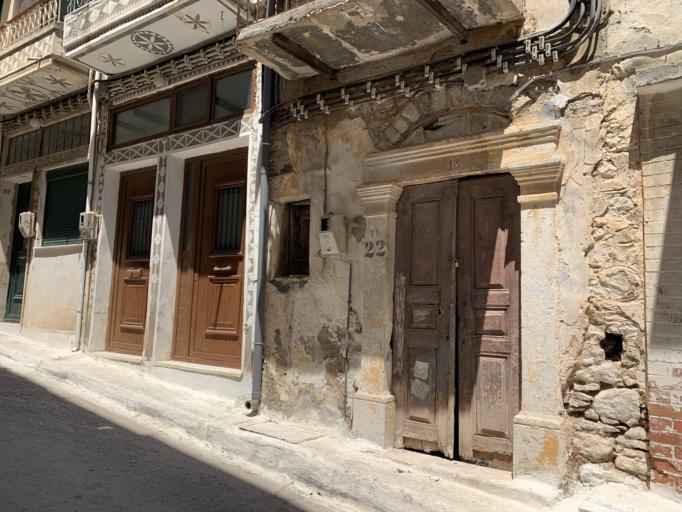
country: GR
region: North Aegean
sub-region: Chios
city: Thymiana
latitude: 38.2271
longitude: 25.9998
